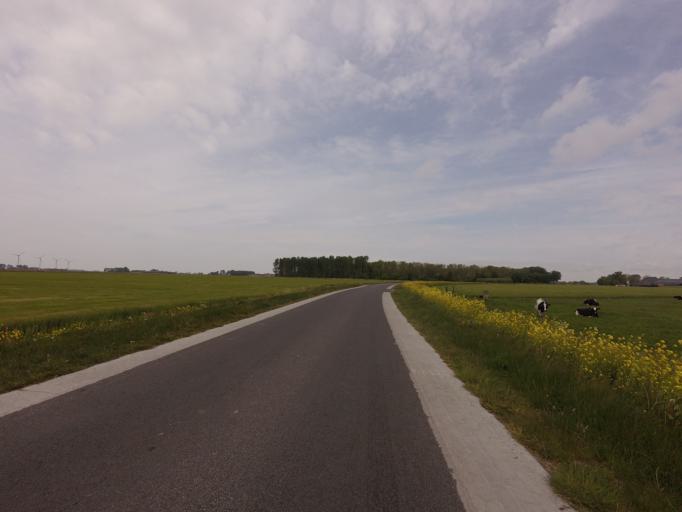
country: NL
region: Friesland
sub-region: Sudwest Fryslan
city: Bolsward
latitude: 53.0917
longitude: 5.4784
